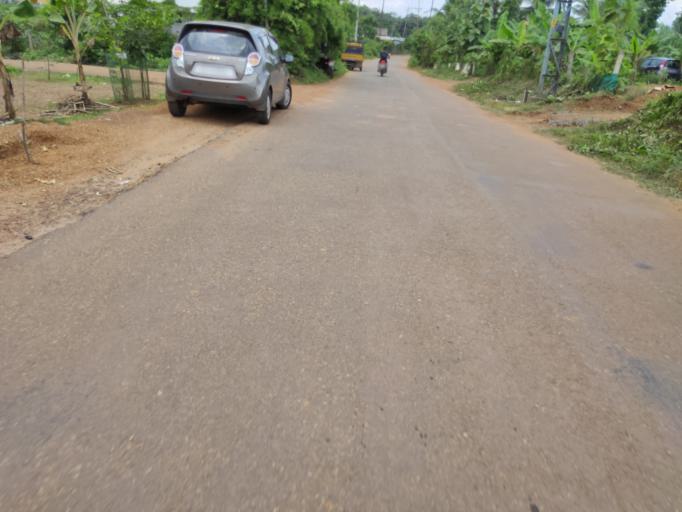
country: IN
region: Kerala
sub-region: Malappuram
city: Manjeri
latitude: 11.2378
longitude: 76.2859
